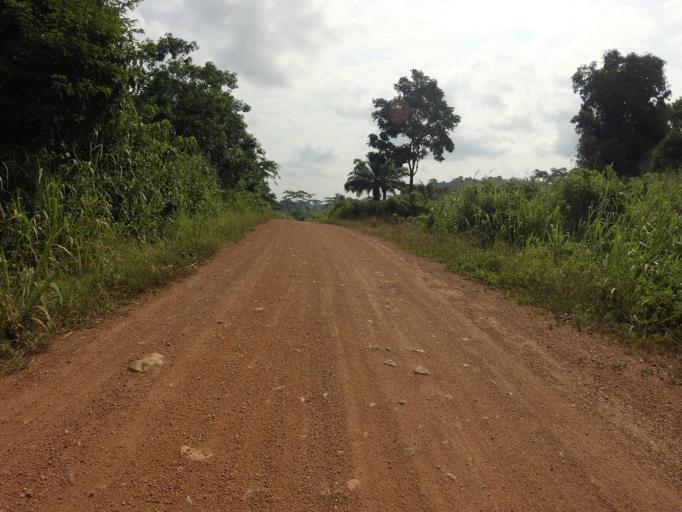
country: GH
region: Volta
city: Kpandu
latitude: 6.8761
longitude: 0.4345
